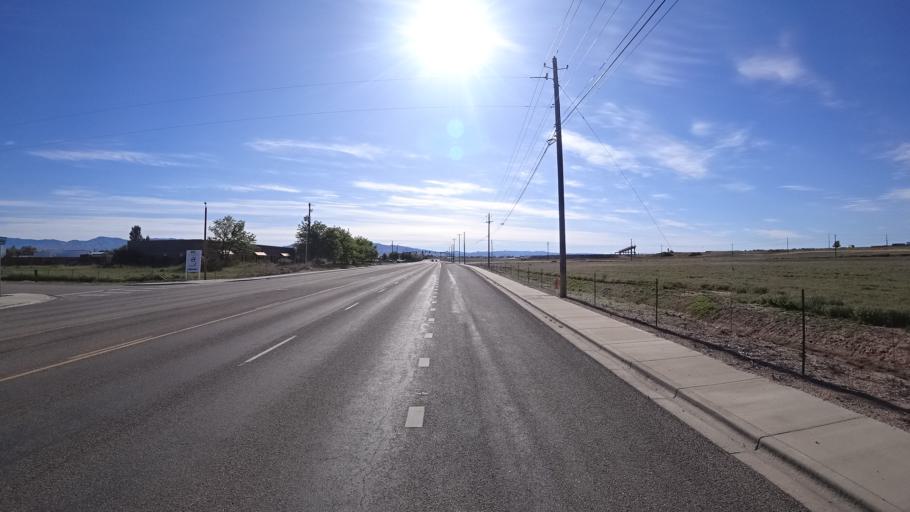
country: US
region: Idaho
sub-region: Ada County
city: Garden City
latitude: 43.5753
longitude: -116.2567
